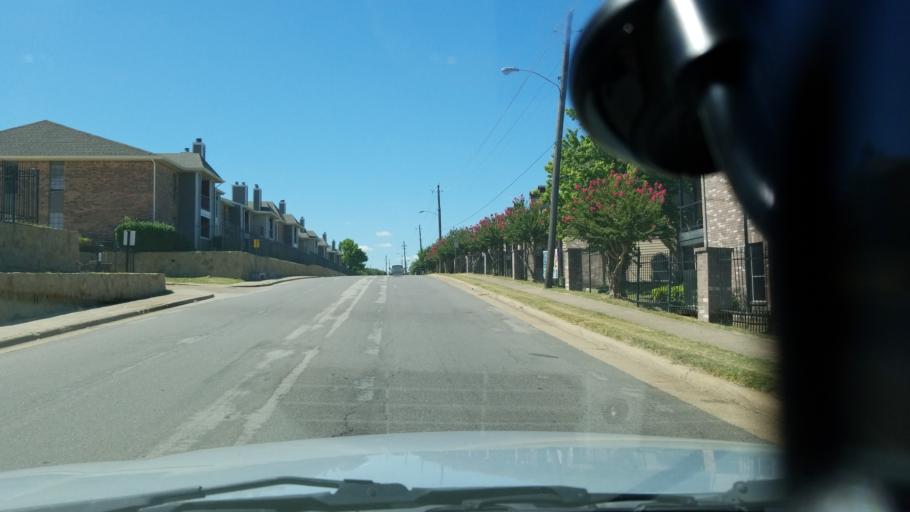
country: US
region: Texas
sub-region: Dallas County
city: Duncanville
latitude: 32.6566
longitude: -96.8698
